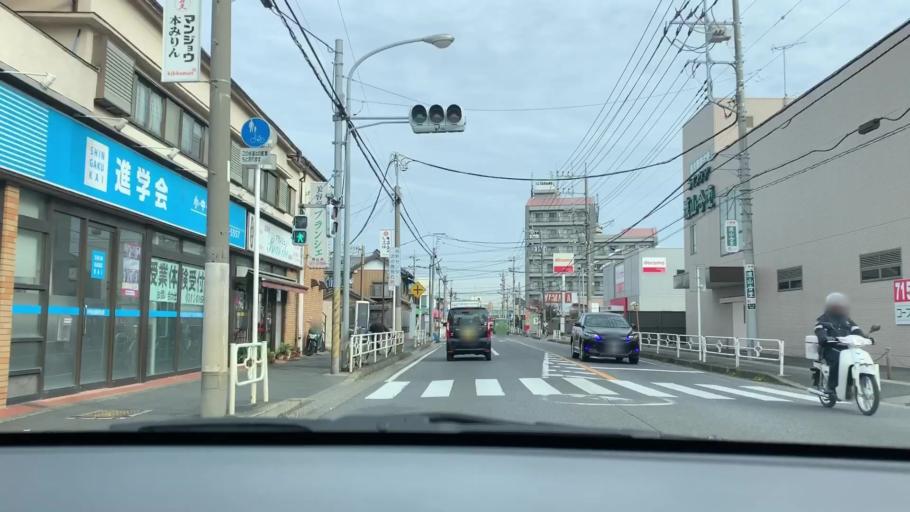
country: JP
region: Chiba
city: Nagareyama
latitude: 35.8506
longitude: 139.8984
